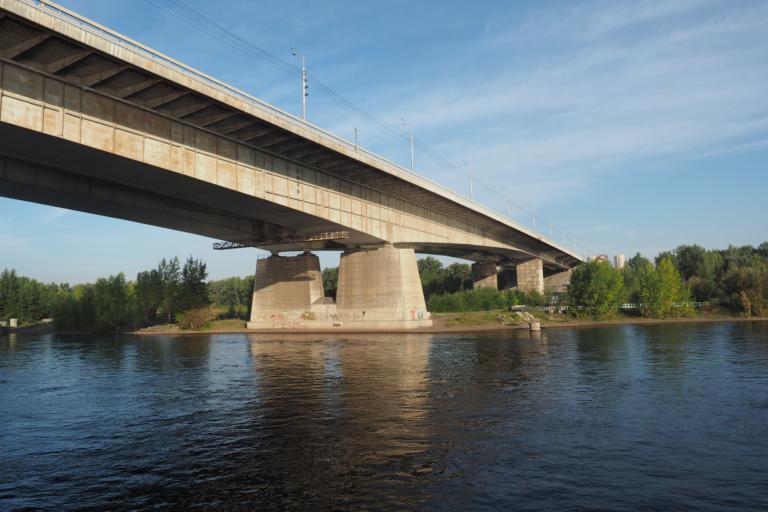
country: RU
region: Krasnoyarskiy
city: Krasnoyarsk
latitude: 56.0205
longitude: 92.9498
